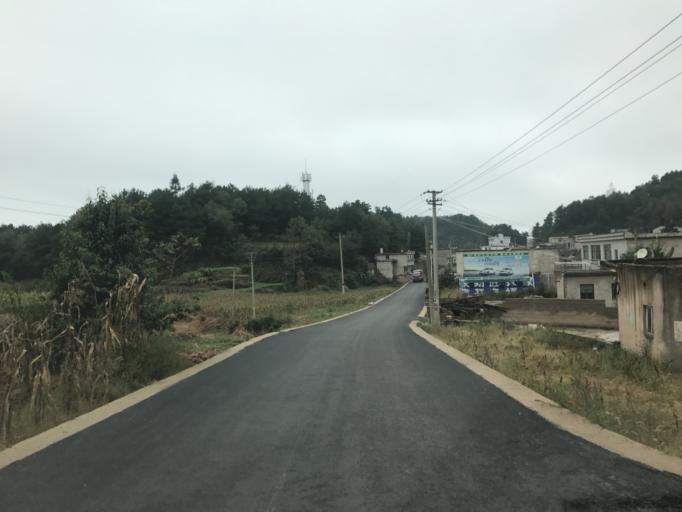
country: CN
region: Guizhou Sheng
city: Supu
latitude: 26.7310
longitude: 106.4377
